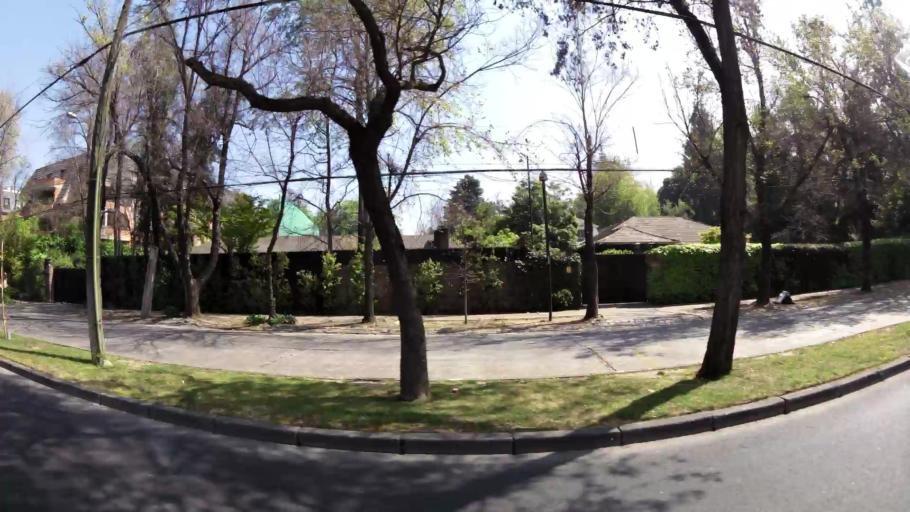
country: CL
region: Santiago Metropolitan
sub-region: Provincia de Santiago
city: Villa Presidente Frei, Nunoa, Santiago, Chile
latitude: -33.3909
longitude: -70.5796
